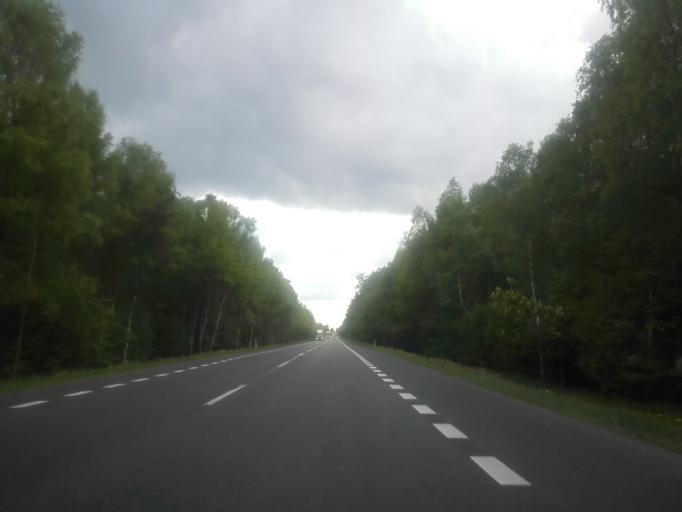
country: PL
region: Masovian Voivodeship
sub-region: Powiat ostrowski
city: Ostrow Mazowiecka
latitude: 52.8355
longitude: 21.9532
